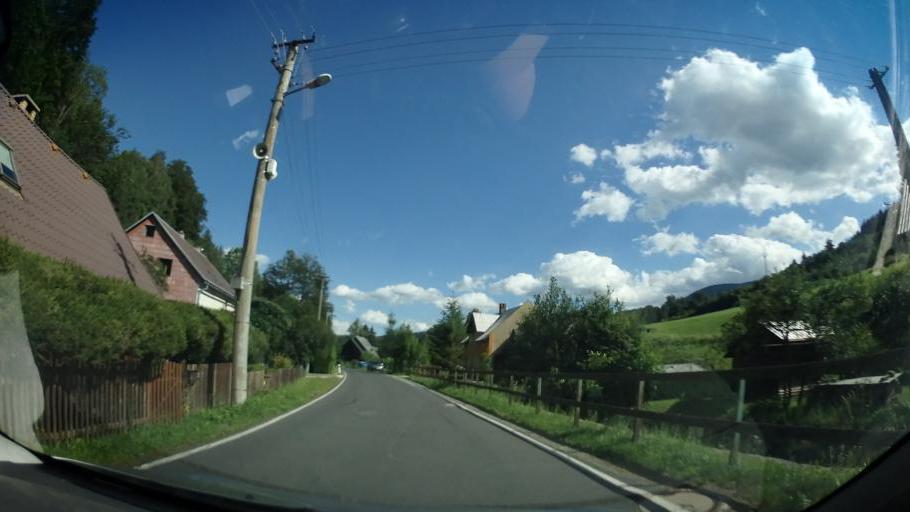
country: CZ
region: Olomoucky
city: Vapenna
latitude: 50.2261
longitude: 17.0860
